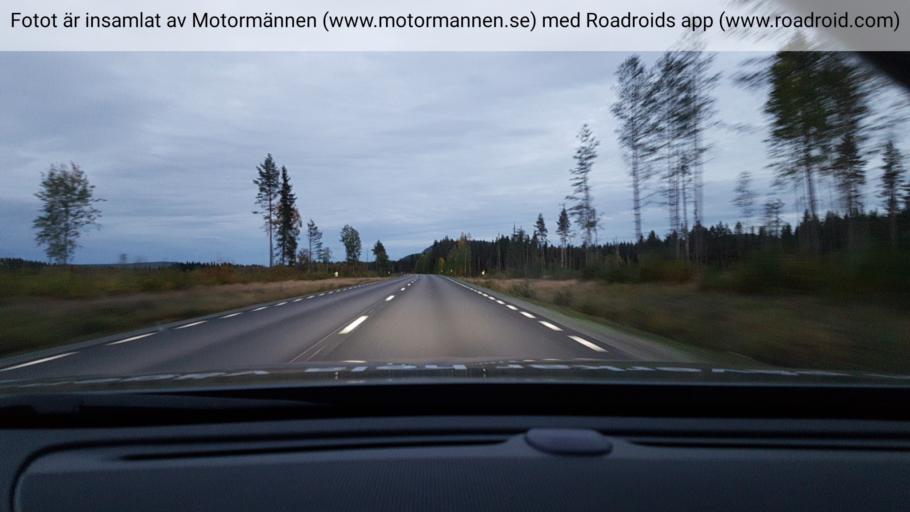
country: SE
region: Norrbotten
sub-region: Alvsbyns Kommun
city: AElvsbyn
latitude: 65.7629
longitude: 20.8754
